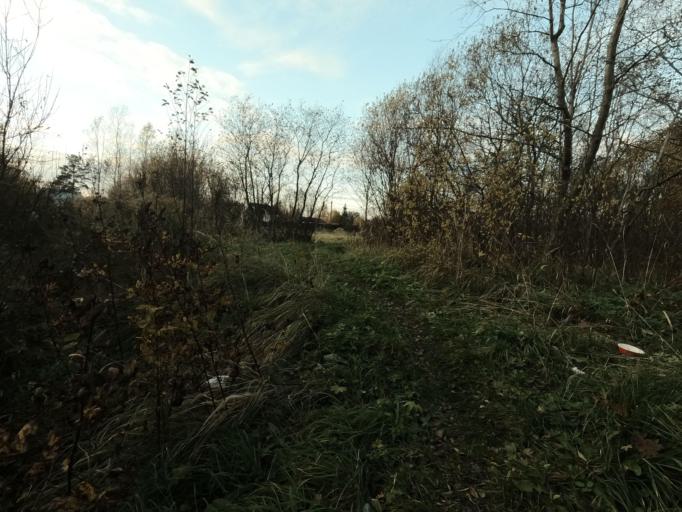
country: RU
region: Leningrad
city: Mga
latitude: 59.7745
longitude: 31.2169
